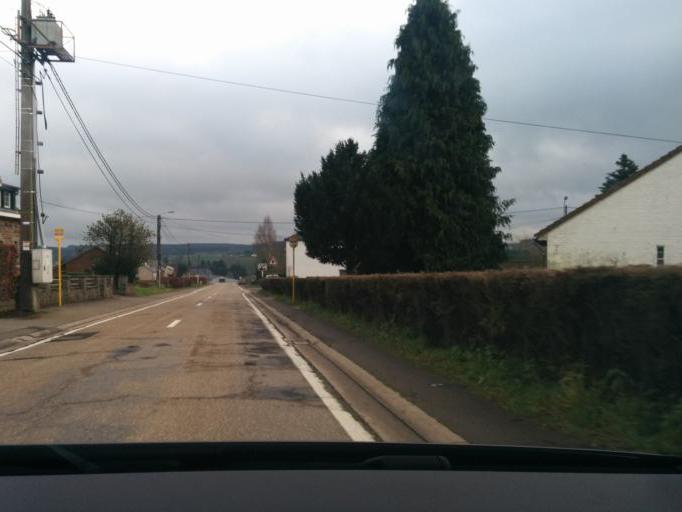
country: BE
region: Wallonia
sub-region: Province du Luxembourg
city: Gouvy
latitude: 50.1885
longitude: 5.9627
